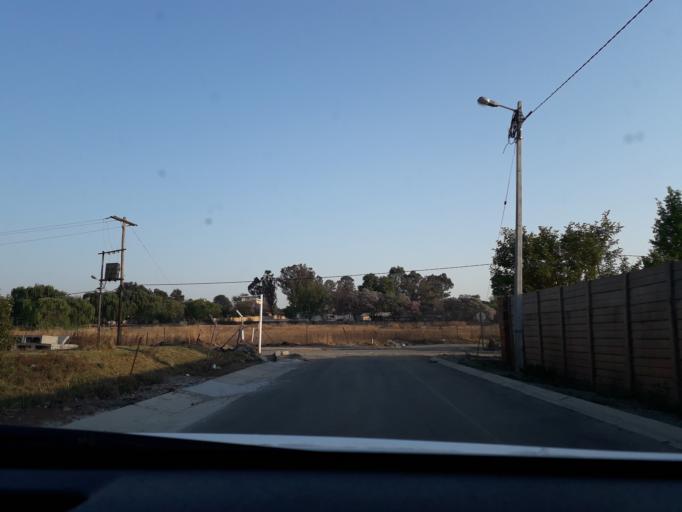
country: ZA
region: Gauteng
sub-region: Ekurhuleni Metropolitan Municipality
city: Benoni
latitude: -26.1135
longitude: 28.3070
